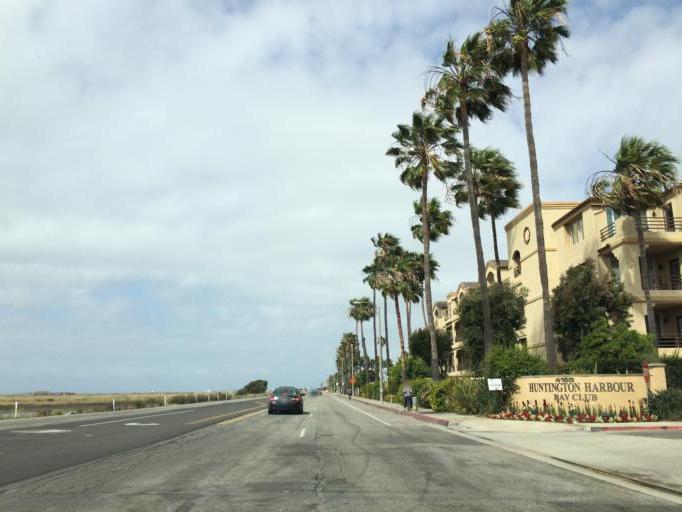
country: US
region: California
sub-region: Orange County
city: Seal Beach
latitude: 33.7117
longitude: -118.0540
